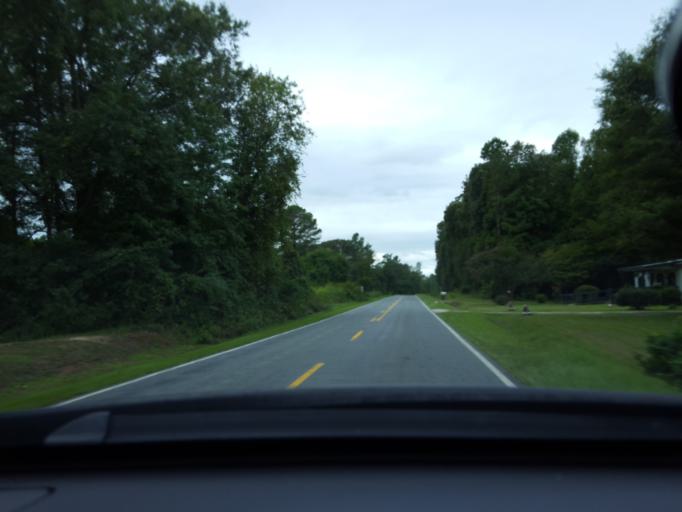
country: US
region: North Carolina
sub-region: Sampson County
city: Clinton
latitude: 34.7775
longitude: -78.3503
